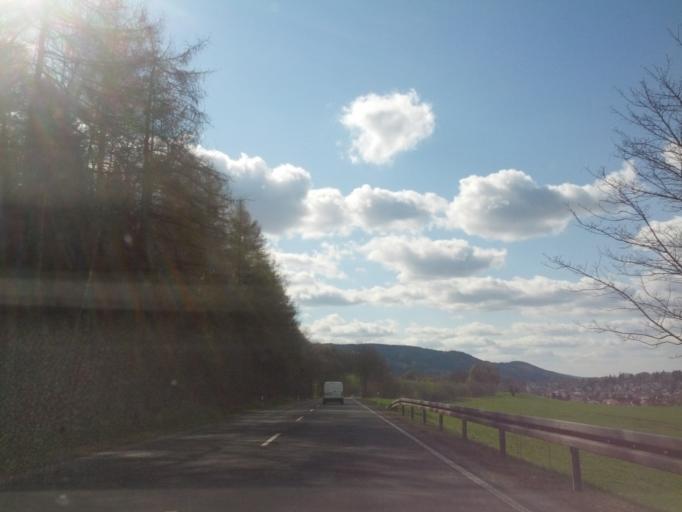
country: DE
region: Thuringia
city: Finsterbergen
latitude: 50.8526
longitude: 10.5947
